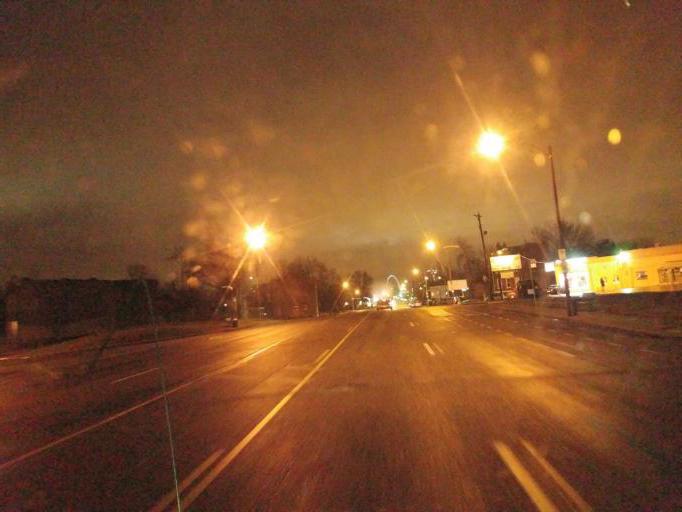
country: US
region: Missouri
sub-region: City of Saint Louis
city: St. Louis
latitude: 38.6539
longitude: -90.2019
